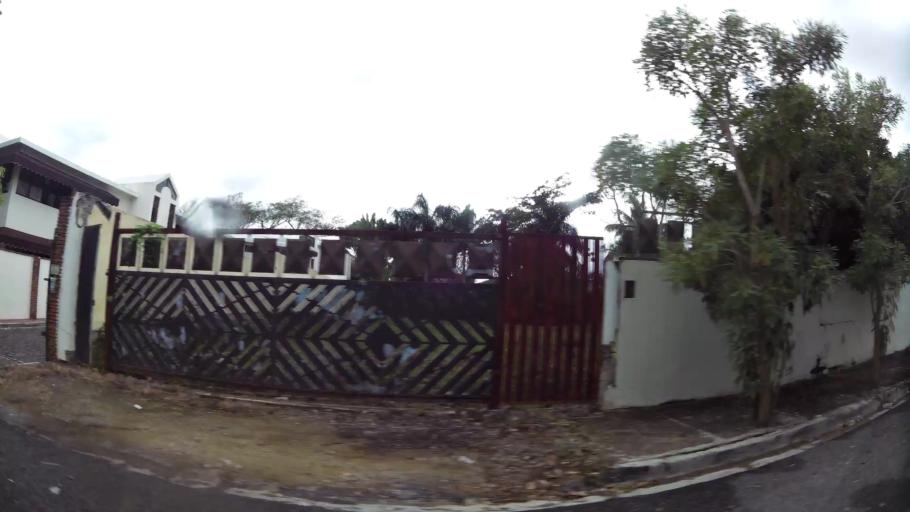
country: DO
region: Nacional
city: La Agustina
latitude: 18.5107
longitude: -69.9482
